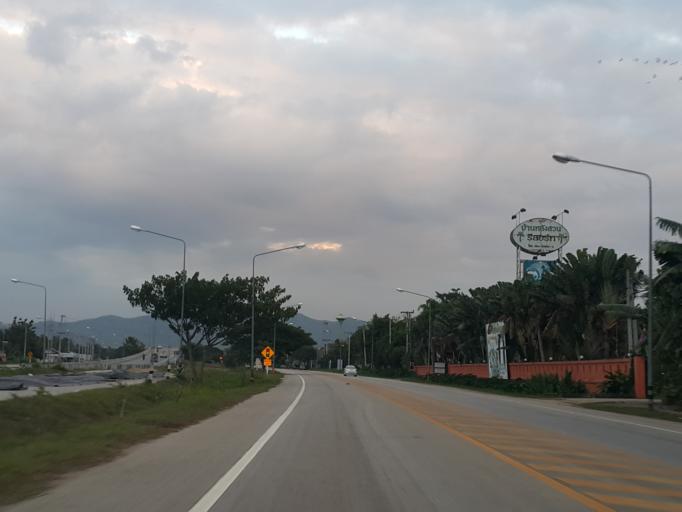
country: TH
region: Lampang
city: Lampang
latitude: 18.2528
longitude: 99.4861
